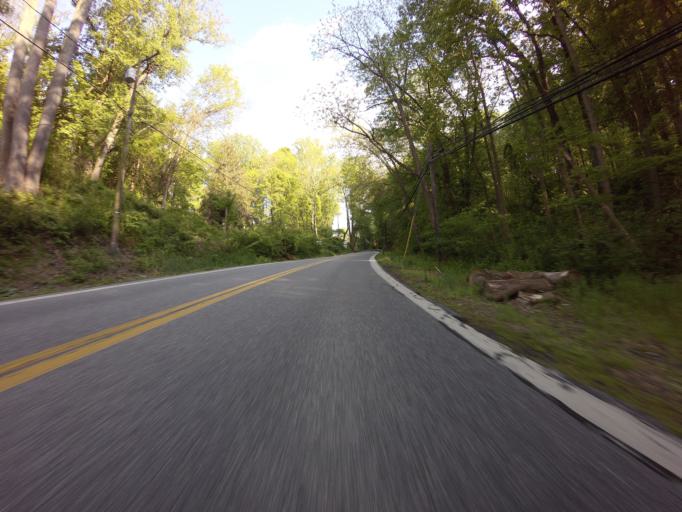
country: US
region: Maryland
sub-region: Baltimore County
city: Mays Chapel
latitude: 39.4606
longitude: -76.6982
